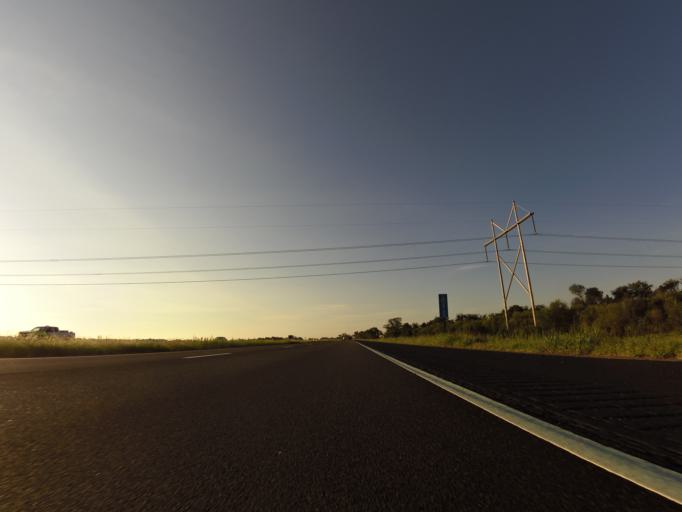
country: US
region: Kansas
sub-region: Sedgwick County
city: Maize
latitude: 37.8080
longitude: -97.4995
